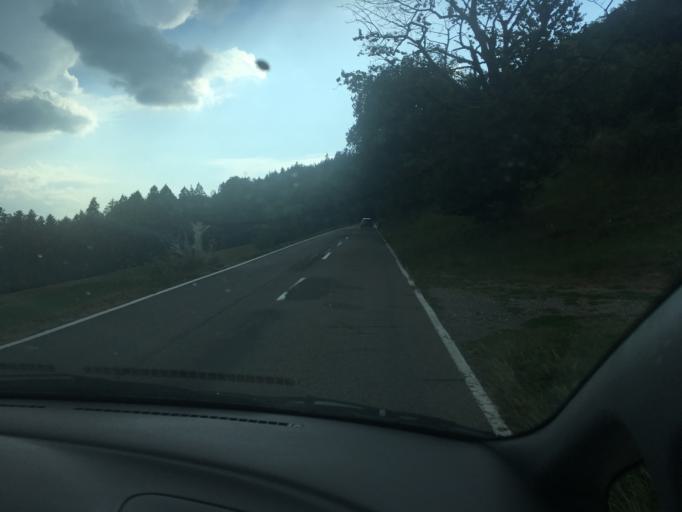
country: CH
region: Bern
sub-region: Bern-Mittelland District
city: Wohlen
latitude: 47.0065
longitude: 7.3526
